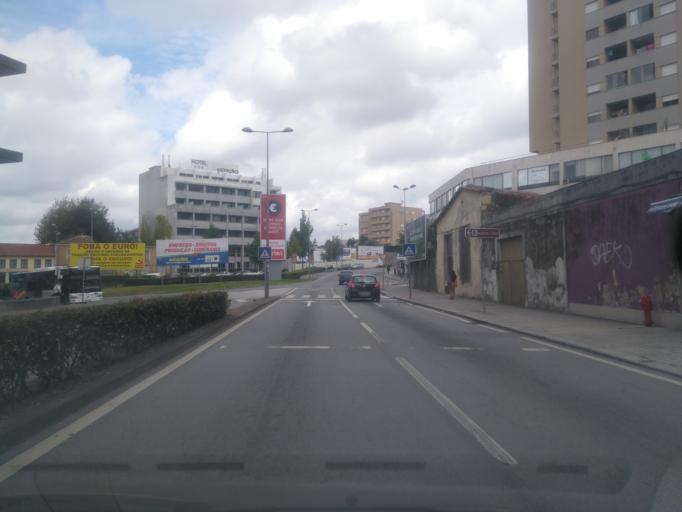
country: PT
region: Braga
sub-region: Braga
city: Braga
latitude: 41.5486
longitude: -8.4336
